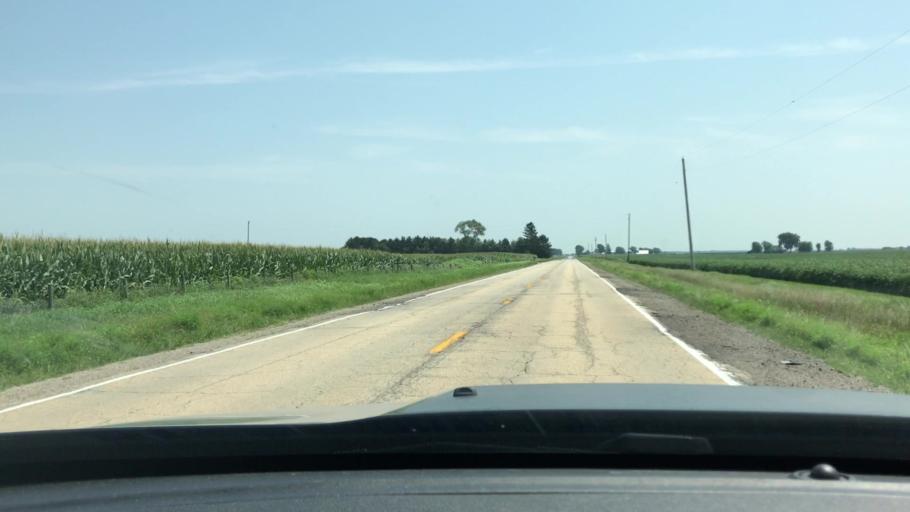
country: US
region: Illinois
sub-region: LaSalle County
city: Ottawa
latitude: 41.4702
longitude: -88.8617
